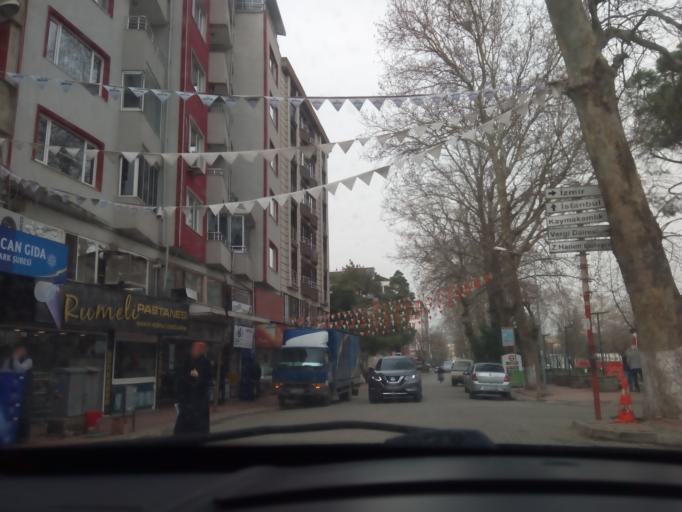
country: TR
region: Balikesir
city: Susurluk
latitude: 39.9164
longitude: 28.1562
